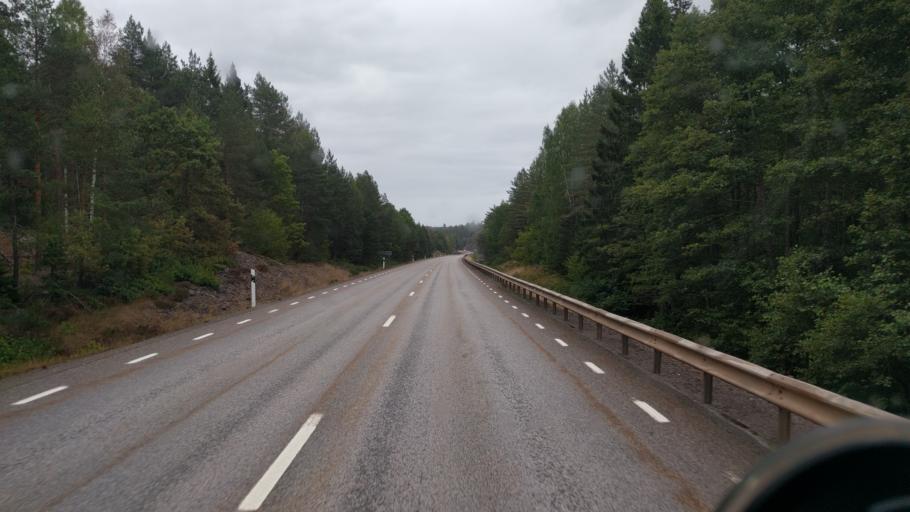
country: SE
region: Kalmar
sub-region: Vasterviks Kommun
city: Ankarsrum
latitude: 57.6981
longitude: 16.2739
